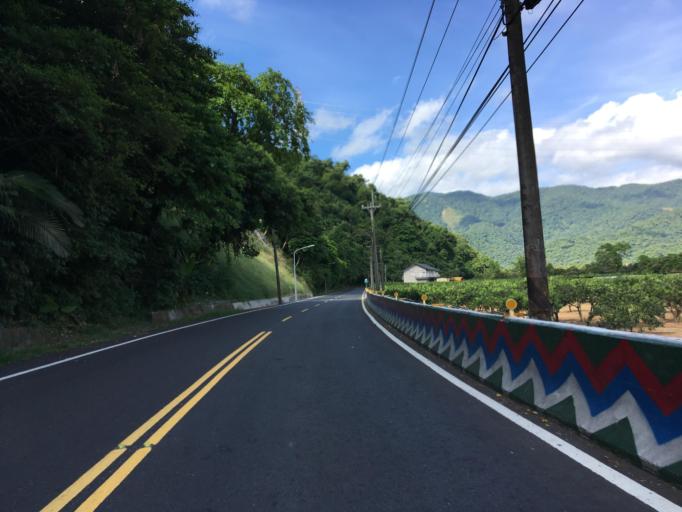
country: TW
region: Taiwan
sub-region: Yilan
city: Yilan
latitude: 24.6182
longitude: 121.6979
